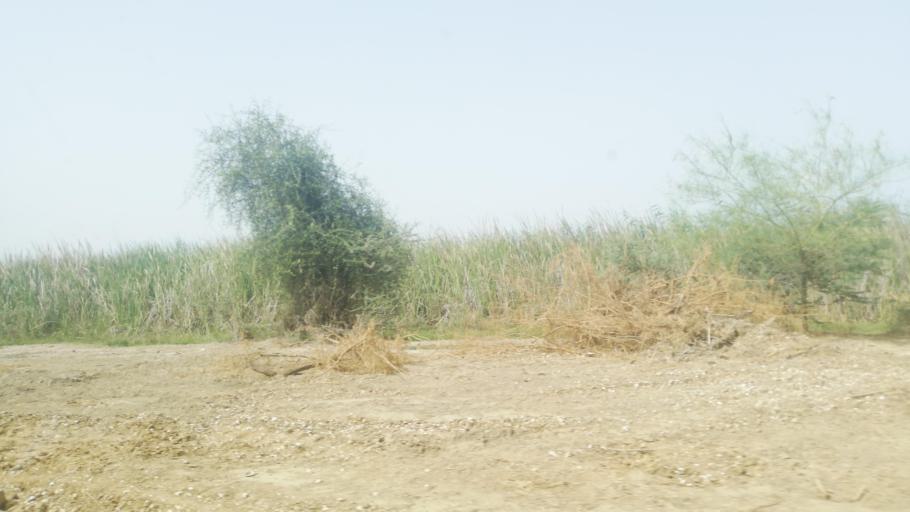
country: SN
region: Saint-Louis
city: Saint-Louis
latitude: 16.0627
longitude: -16.3141
